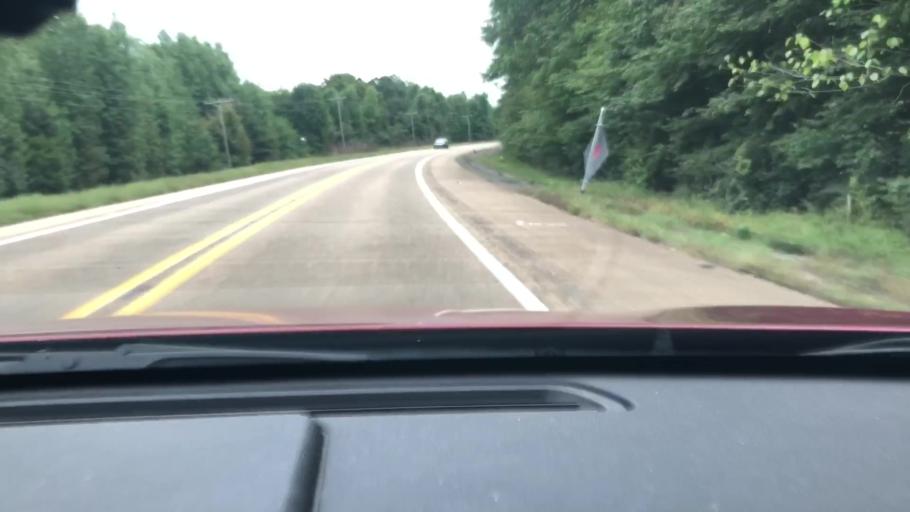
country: US
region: Arkansas
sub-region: Miller County
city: Texarkana
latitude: 33.4186
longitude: -93.8156
